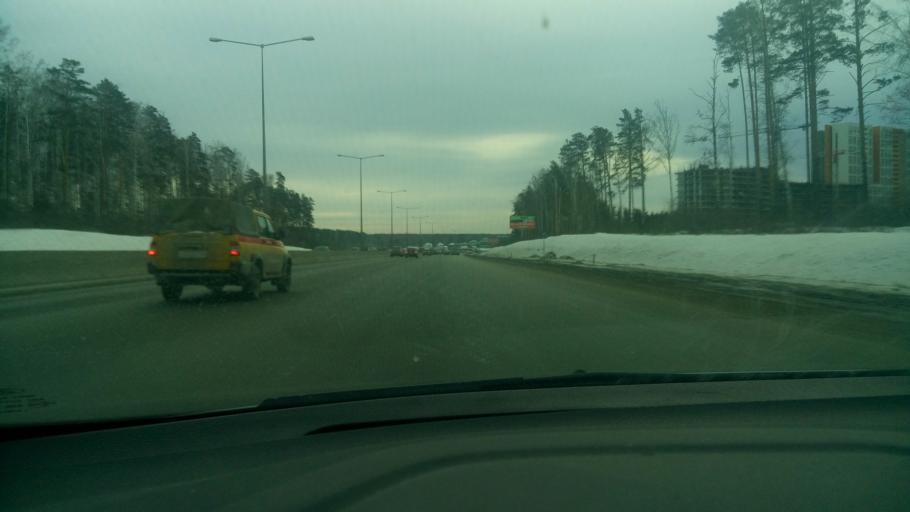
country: RU
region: Sverdlovsk
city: Istok
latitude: 56.7822
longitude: 60.6992
